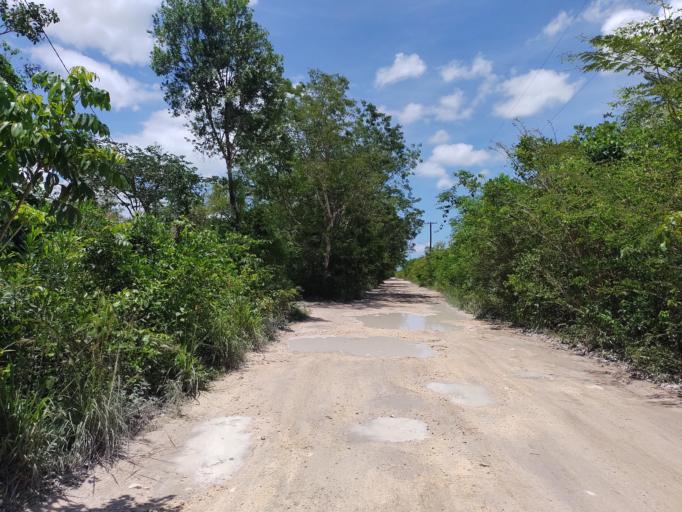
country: MX
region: Quintana Roo
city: San Miguel de Cozumel
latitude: 20.4923
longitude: -86.9061
